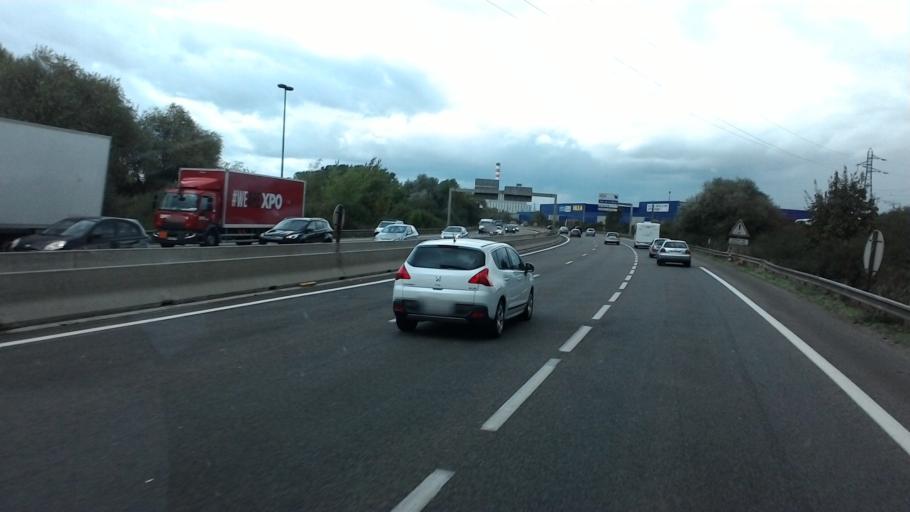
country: FR
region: Lorraine
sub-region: Departement de la Moselle
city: Saint-Julien-les-Metz
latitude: 49.1418
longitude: 6.1835
